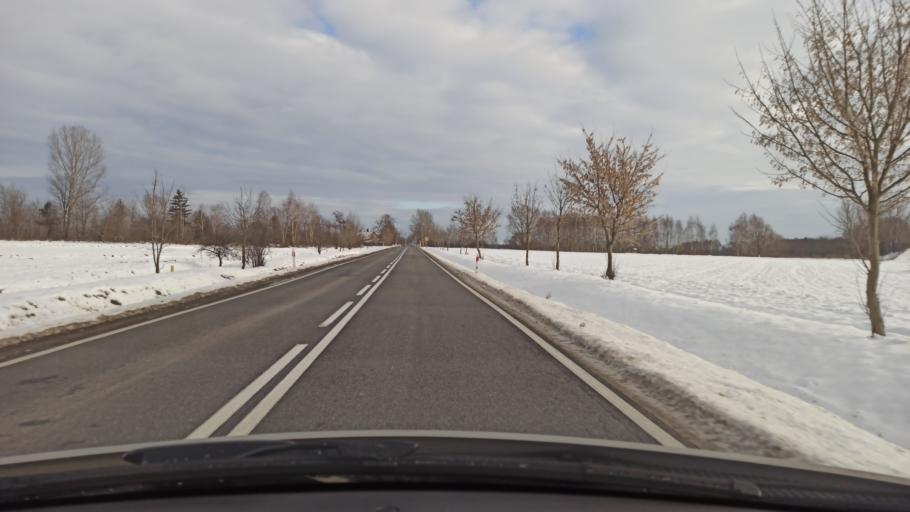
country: PL
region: Subcarpathian Voivodeship
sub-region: Powiat lezajski
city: Wierzawice
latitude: 50.2182
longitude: 22.4684
